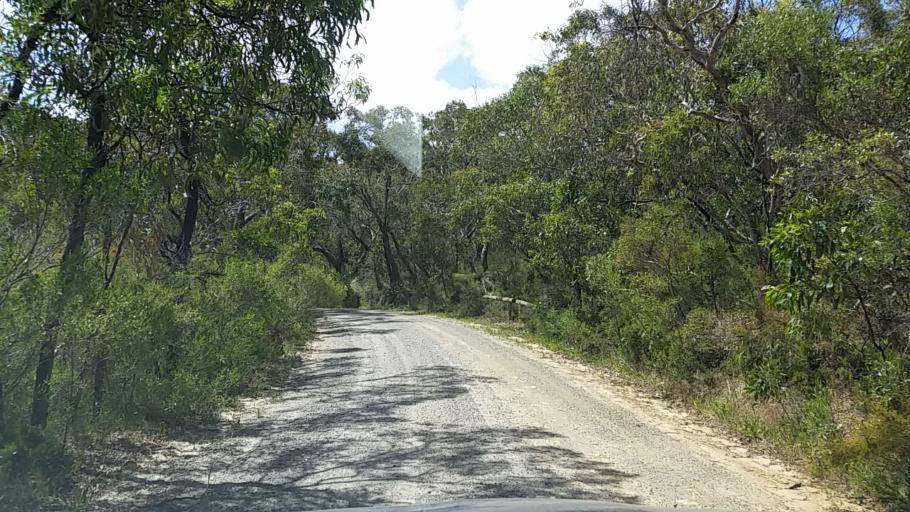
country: AU
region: South Australia
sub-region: Alexandrina
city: Mount Compass
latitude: -35.4420
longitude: 138.5843
